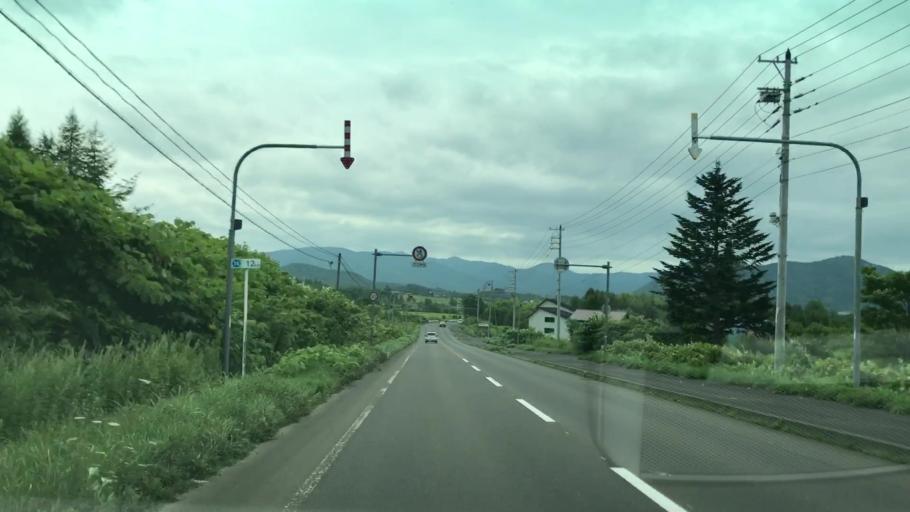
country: JP
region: Hokkaido
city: Yoichi
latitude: 43.1024
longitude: 140.8236
